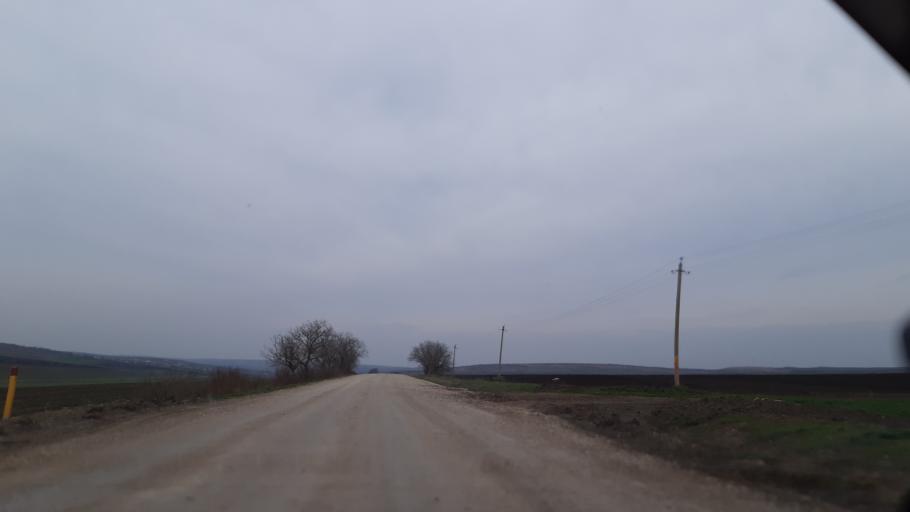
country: MD
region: Soldanesti
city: Soldanesti
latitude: 47.6060
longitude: 28.6528
